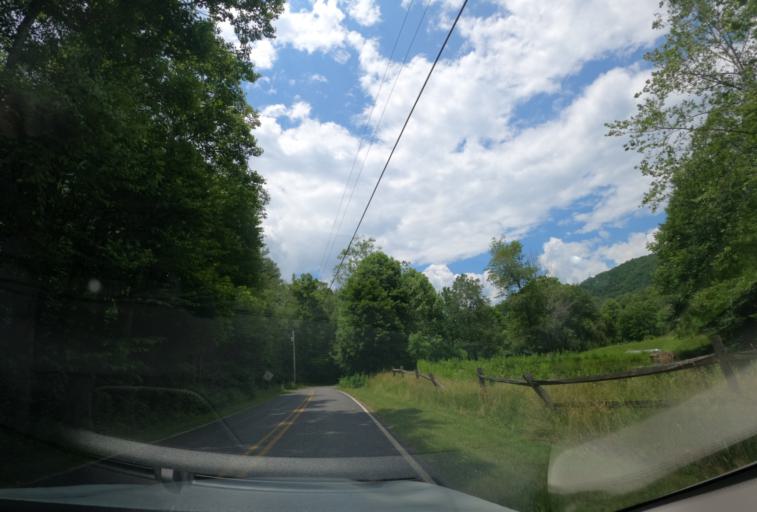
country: US
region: North Carolina
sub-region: Haywood County
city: Hazelwood
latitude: 35.4009
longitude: -82.8980
